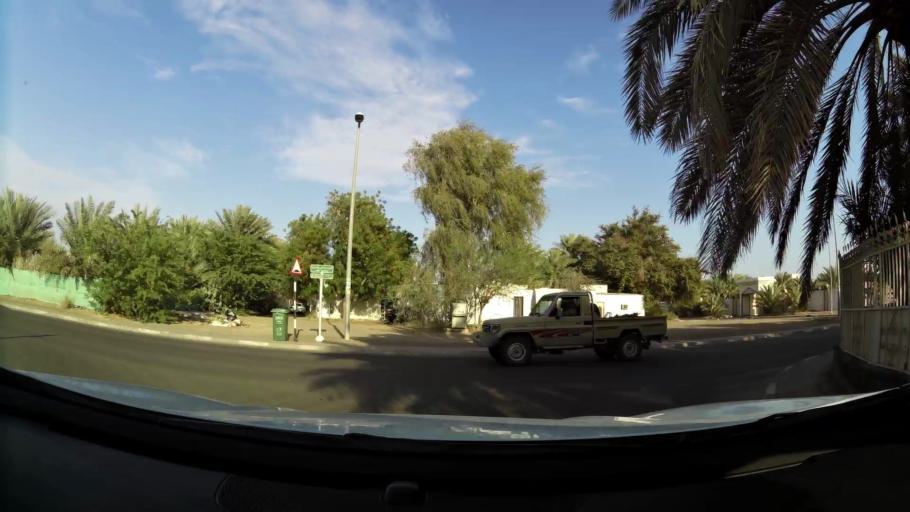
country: AE
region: Abu Dhabi
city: Al Ain
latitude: 24.0823
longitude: 55.8432
